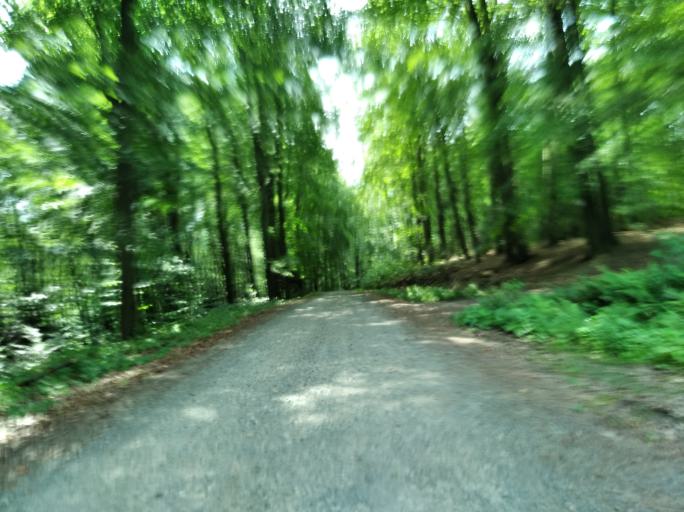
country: PL
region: Subcarpathian Voivodeship
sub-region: Powiat strzyzowski
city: Wisniowa
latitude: 49.8413
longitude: 21.6645
